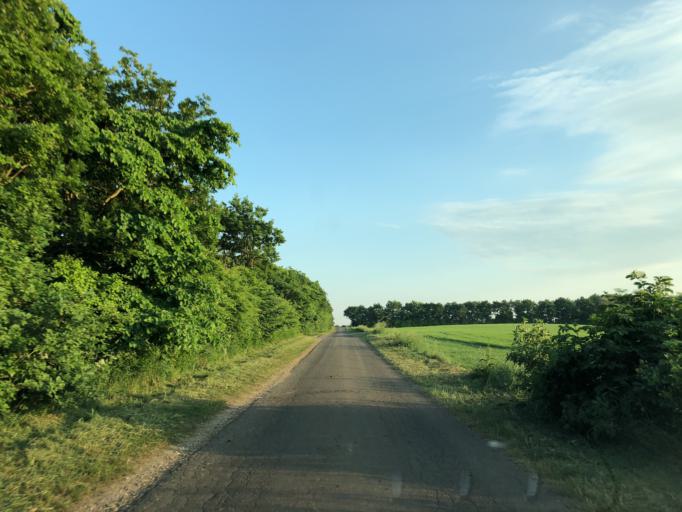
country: DK
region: Central Jutland
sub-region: Struer Kommune
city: Struer
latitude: 56.3988
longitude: 8.4846
